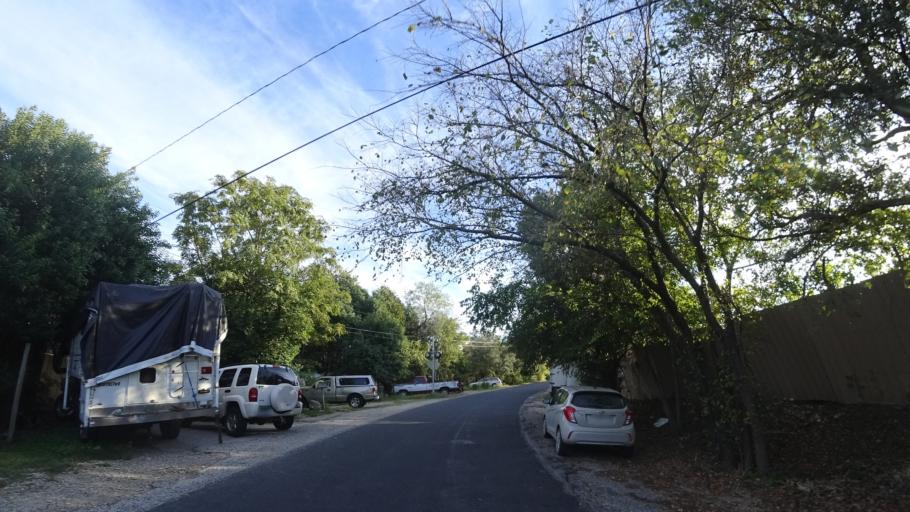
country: US
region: Texas
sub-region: Travis County
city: Austin
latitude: 30.2098
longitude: -97.7709
